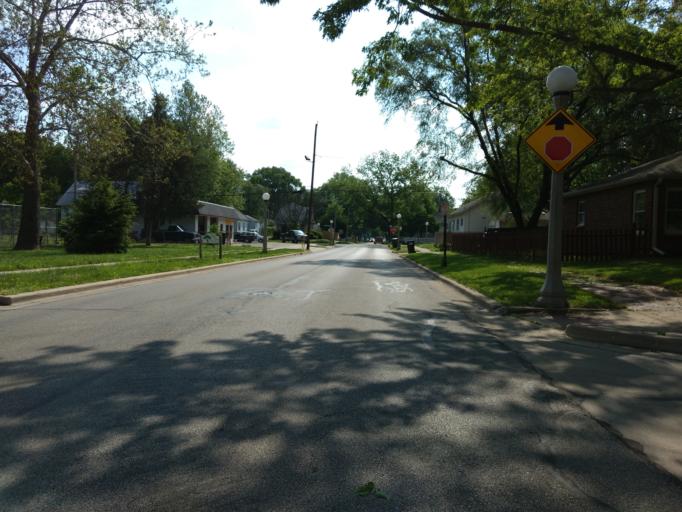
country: US
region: Illinois
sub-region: Champaign County
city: Urbana
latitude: 40.1109
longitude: -88.1969
